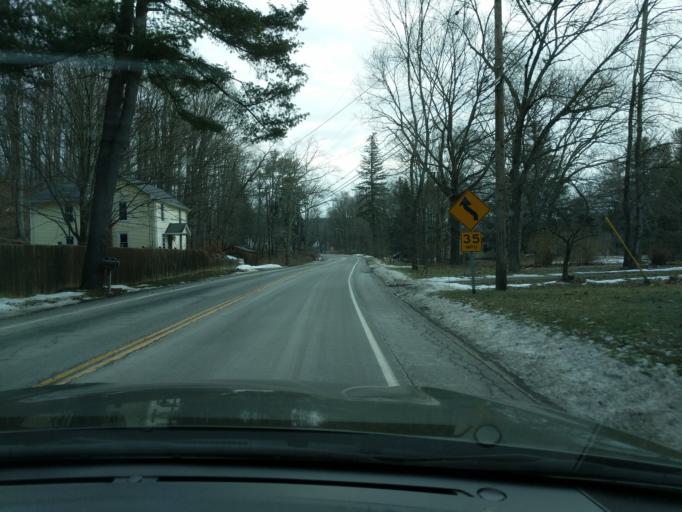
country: US
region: New York
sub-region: Tompkins County
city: East Ithaca
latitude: 42.3871
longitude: -76.4062
